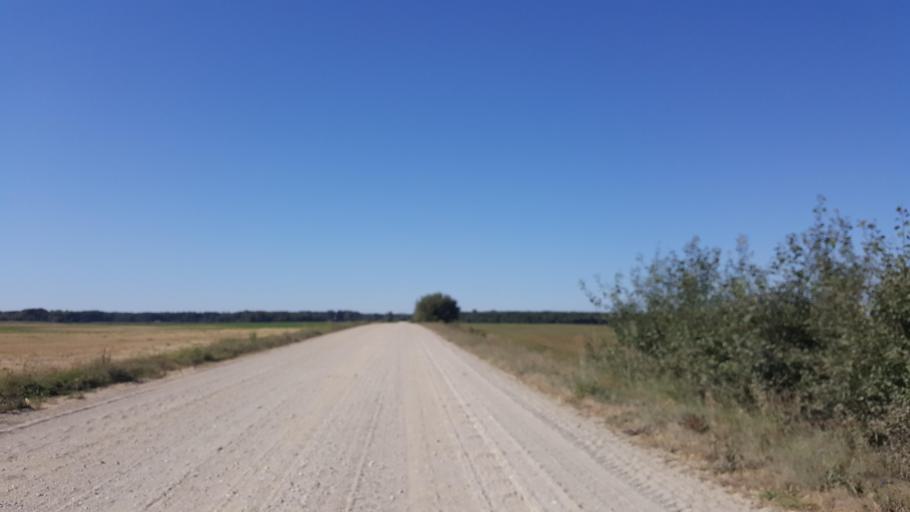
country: BY
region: Brest
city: Charnawchytsy
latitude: 52.3332
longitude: 23.6268
